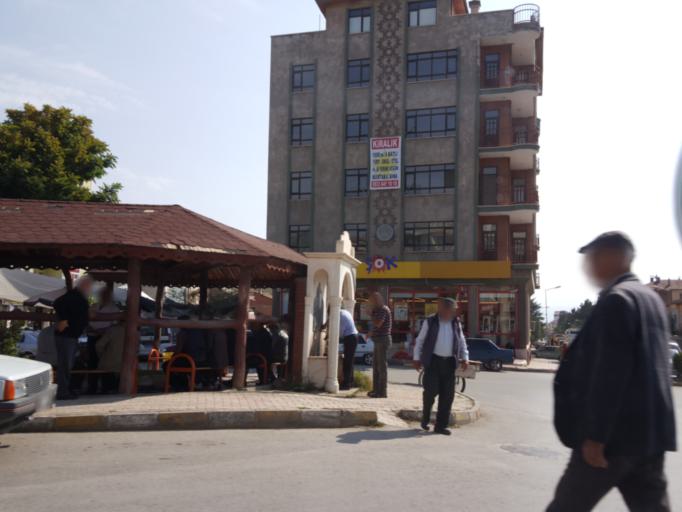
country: TR
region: Tokat
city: Zile
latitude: 40.2990
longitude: 35.8872
